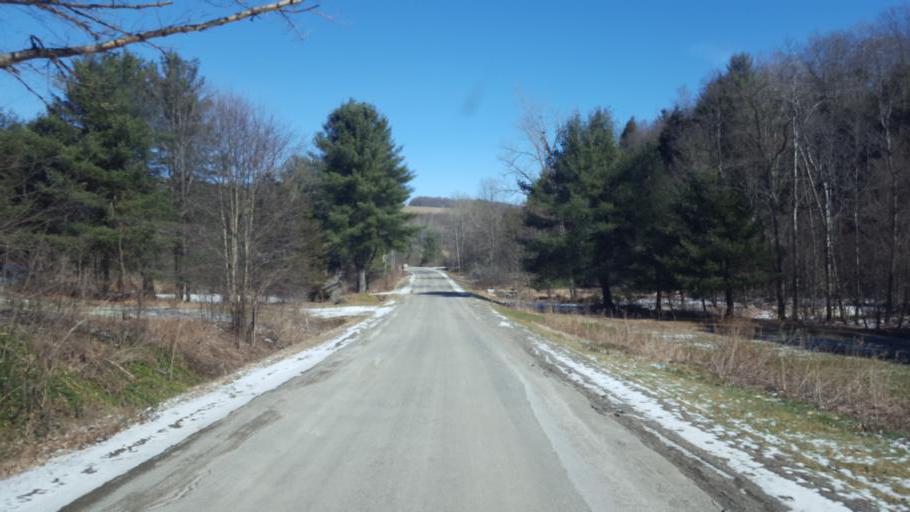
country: US
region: New York
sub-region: Allegany County
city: Wellsville
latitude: 42.0669
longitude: -77.9472
